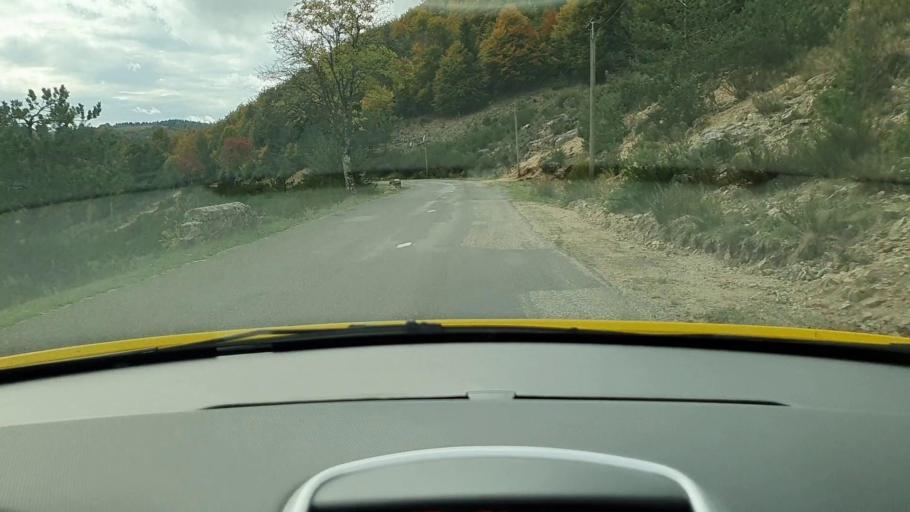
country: FR
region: Languedoc-Roussillon
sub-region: Departement du Gard
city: Valleraugue
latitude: 44.0795
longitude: 3.5260
